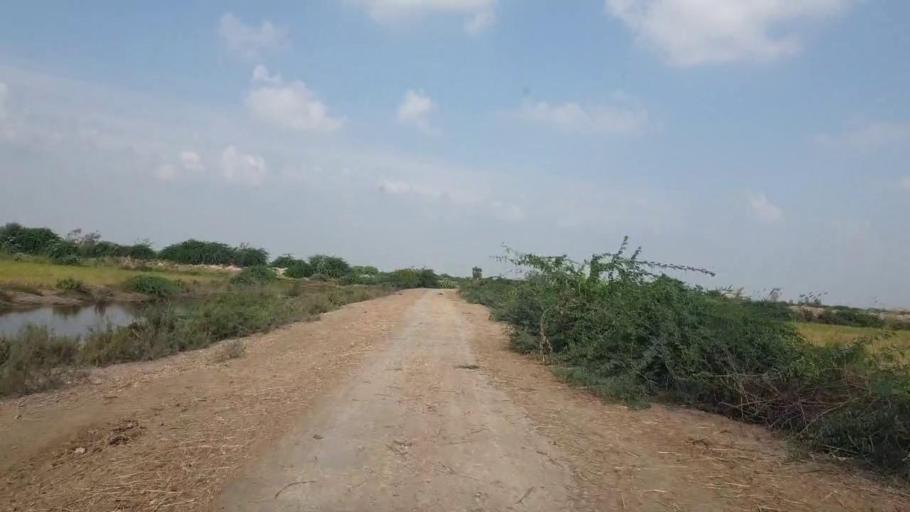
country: PK
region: Sindh
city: Badin
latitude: 24.4763
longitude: 68.5961
